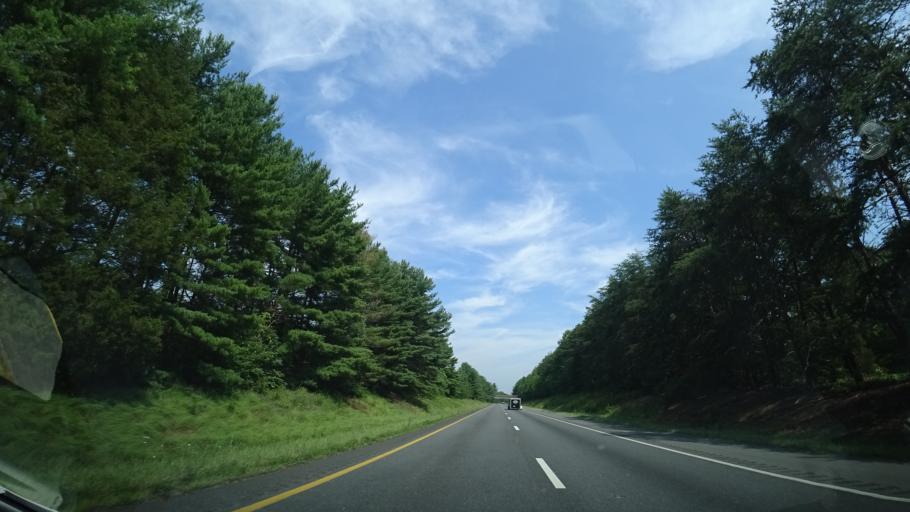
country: US
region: Virginia
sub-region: Louisa County
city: Louisa
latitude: 37.9415
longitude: -78.1122
